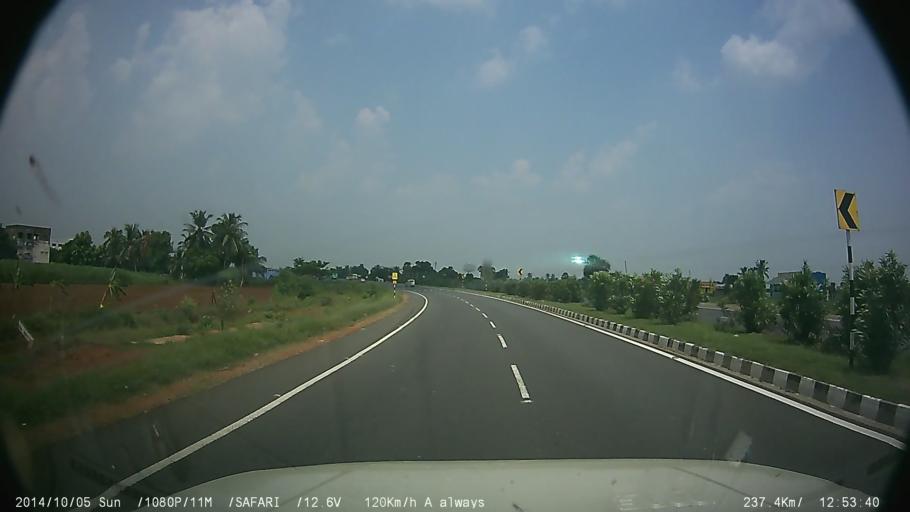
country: IN
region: Tamil Nadu
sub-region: Cuddalore
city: Panruti
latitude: 11.7484
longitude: 79.3724
